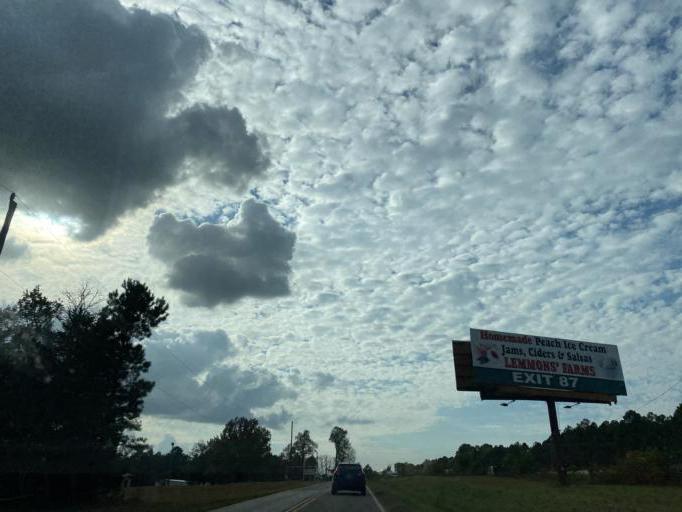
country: US
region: South Carolina
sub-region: Cherokee County
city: Gaffney
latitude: 35.0755
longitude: -81.7337
